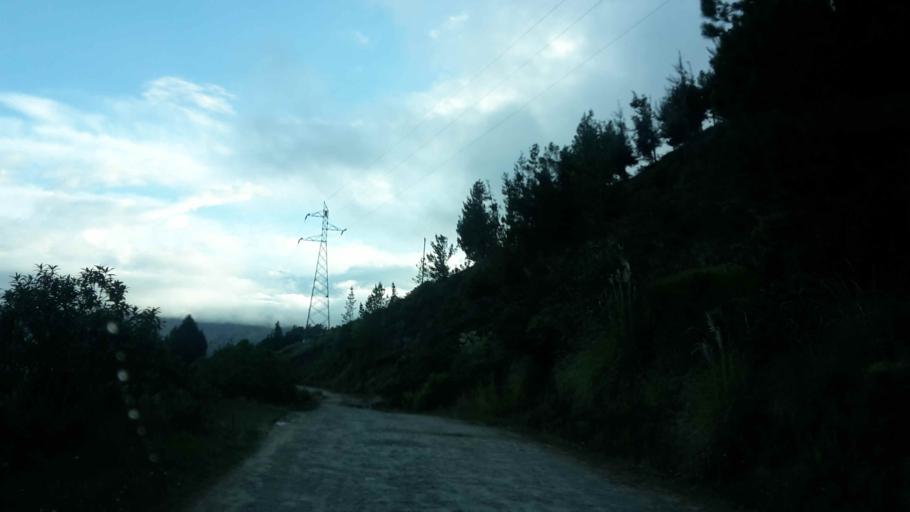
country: BO
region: Cochabamba
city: Colomi
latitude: -17.2568
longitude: -65.9047
